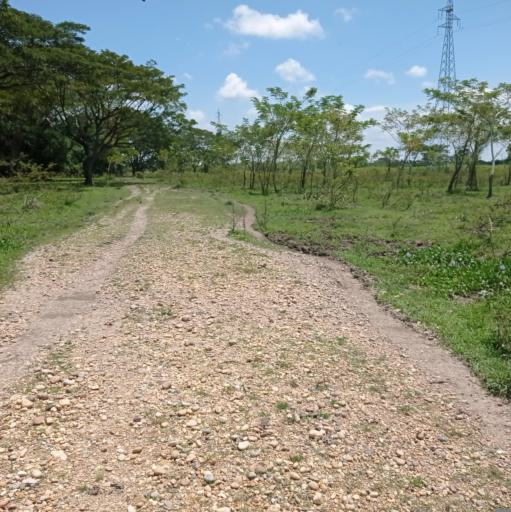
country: CO
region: Santander
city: Barrancabermeja
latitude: 7.1065
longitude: -73.8778
